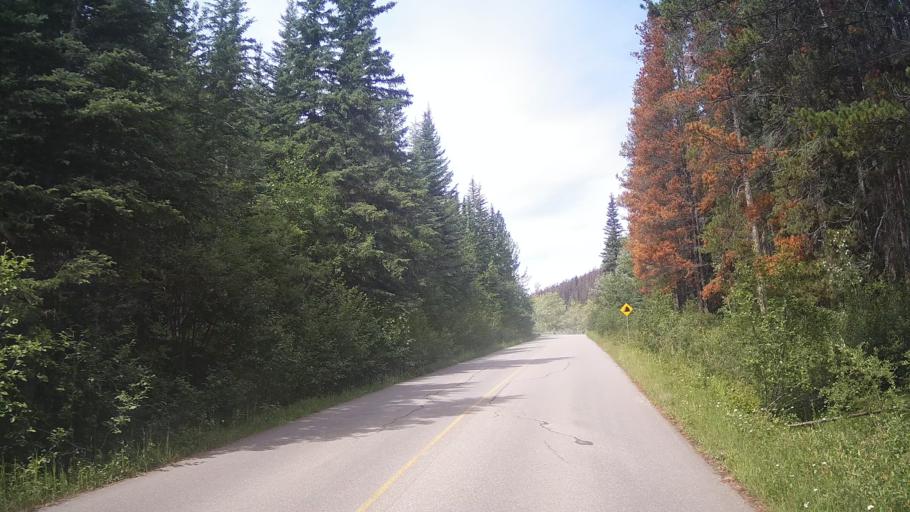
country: CA
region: Alberta
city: Hinton
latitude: 53.1775
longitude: -117.8420
